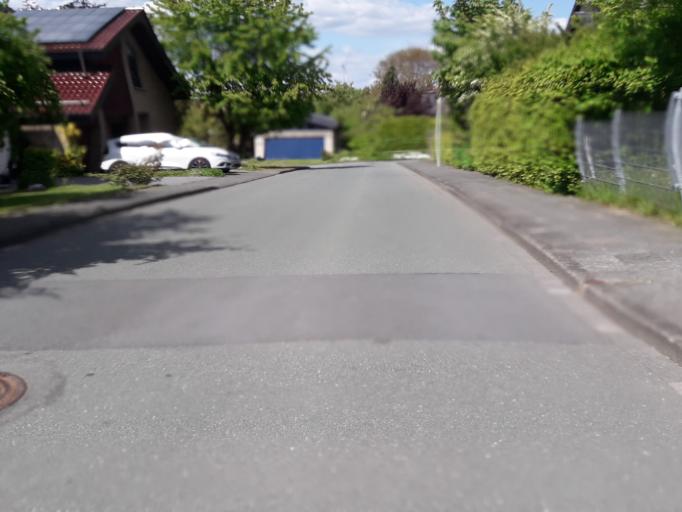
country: DE
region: North Rhine-Westphalia
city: Lichtenau
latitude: 51.6930
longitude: 8.8463
